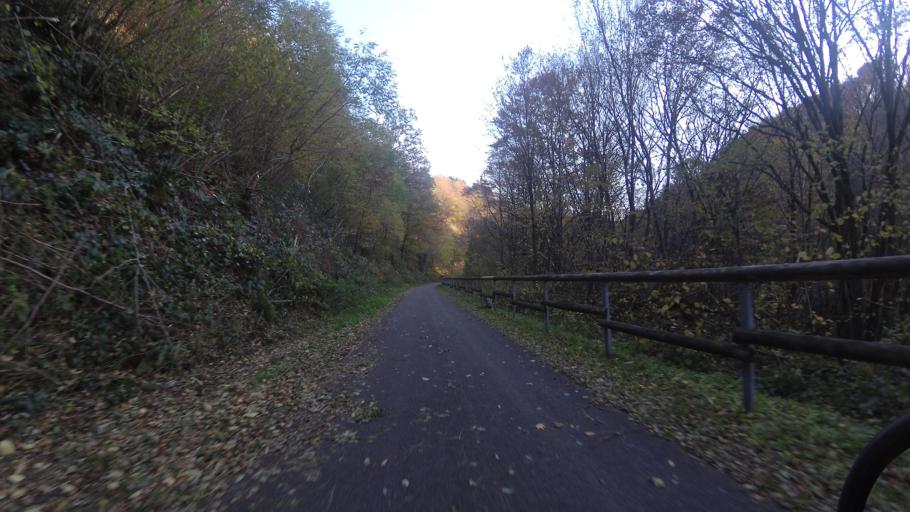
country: DE
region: Rheinland-Pfalz
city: Ollmuth
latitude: 49.6688
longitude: 6.7232
